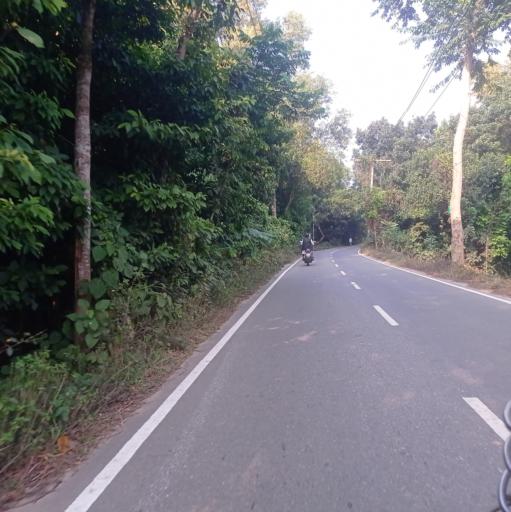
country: BD
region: Dhaka
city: Bhairab Bazar
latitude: 24.0568
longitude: 90.8372
